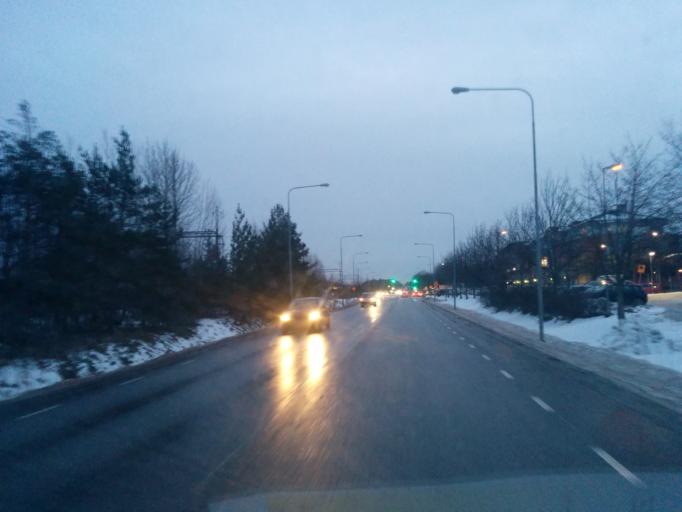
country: SE
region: Stockholm
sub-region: Sollentuna Kommun
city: Sollentuna
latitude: 59.4617
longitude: 17.9233
